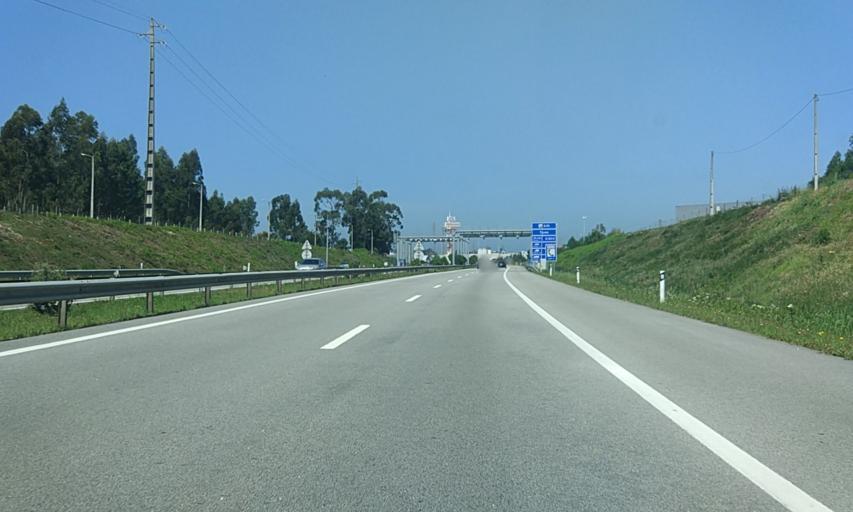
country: PT
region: Aveiro
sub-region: Aveiro
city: Aveiro
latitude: 40.6448
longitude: -8.6097
